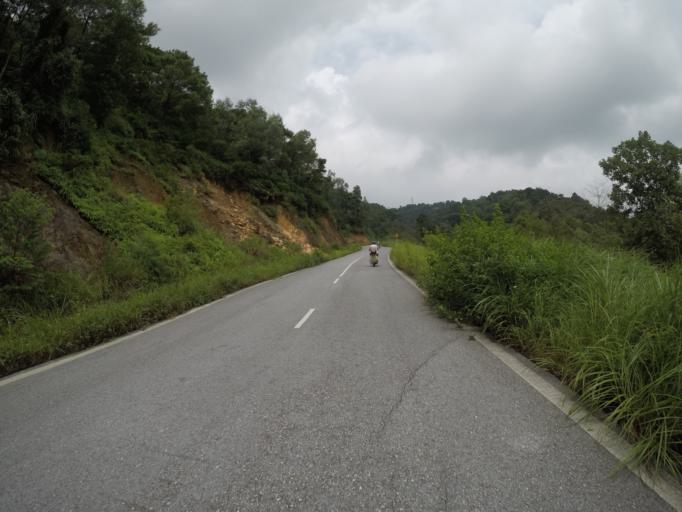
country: VN
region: Ha Noi
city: Soc Son
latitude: 21.2834
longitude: 105.8250
